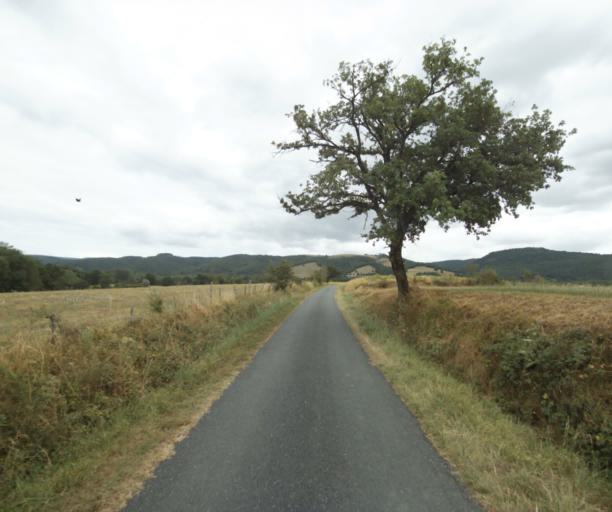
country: FR
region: Midi-Pyrenees
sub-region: Departement du Tarn
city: Soreze
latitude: 43.4648
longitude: 2.0695
